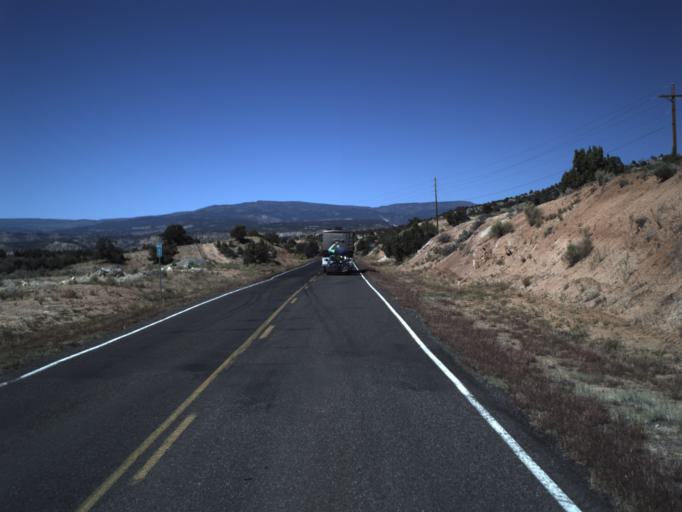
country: US
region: Utah
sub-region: Wayne County
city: Loa
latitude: 37.7487
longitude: -111.5649
